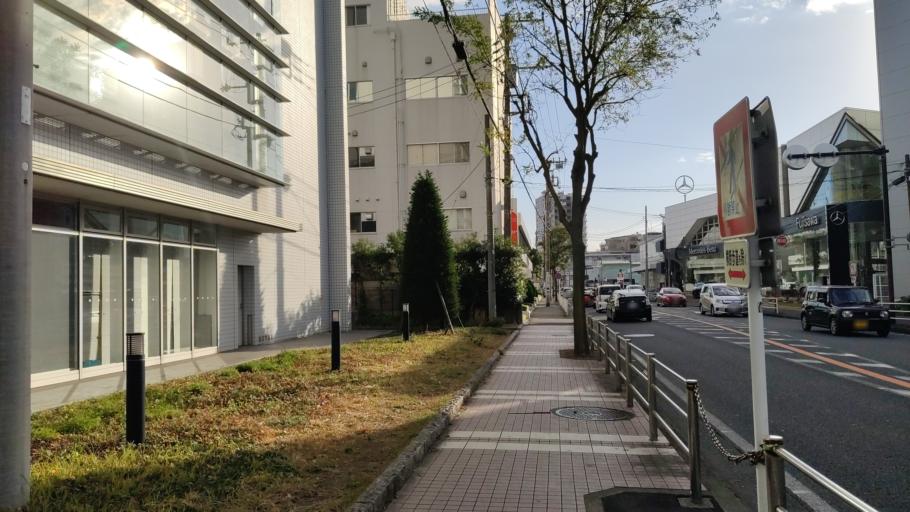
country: JP
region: Kanagawa
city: Fujisawa
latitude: 35.3313
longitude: 139.4883
